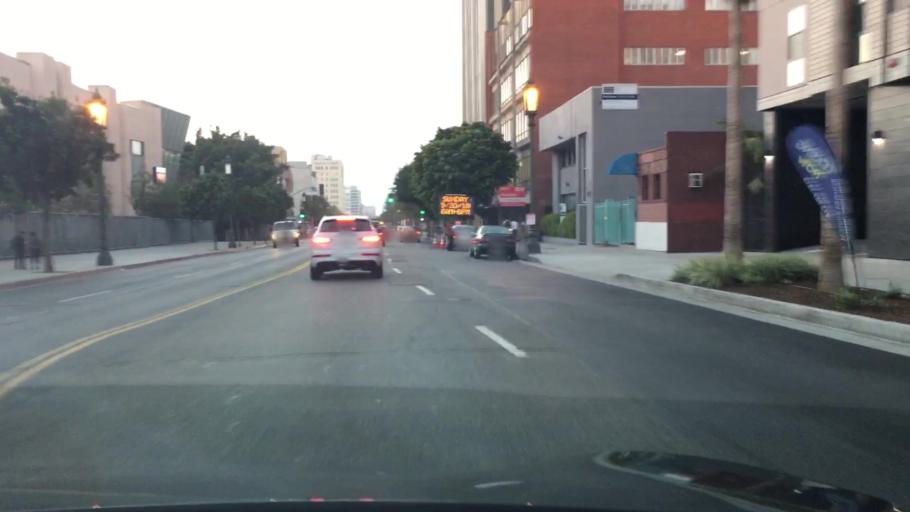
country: US
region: California
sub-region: Los Angeles County
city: Echo Park
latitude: 34.0550
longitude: -118.2690
